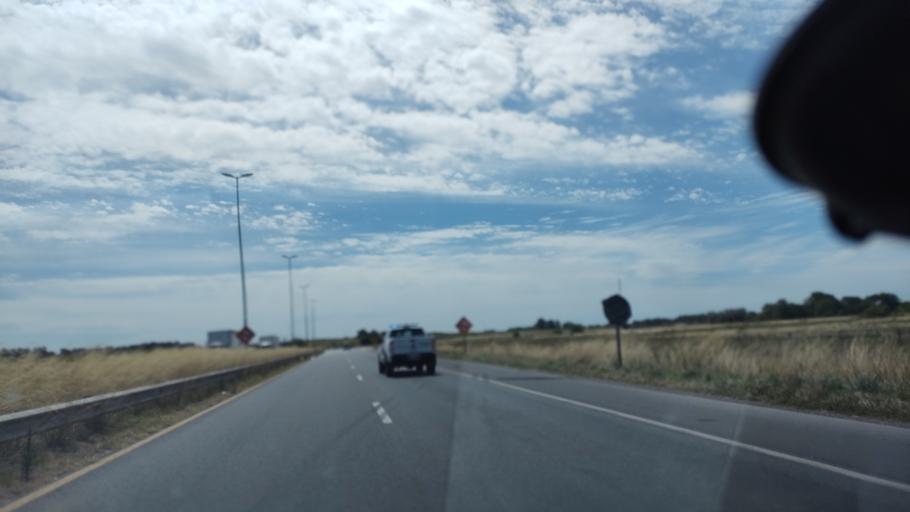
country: AR
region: Buenos Aires
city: Canuelas
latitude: -35.0240
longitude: -58.7374
